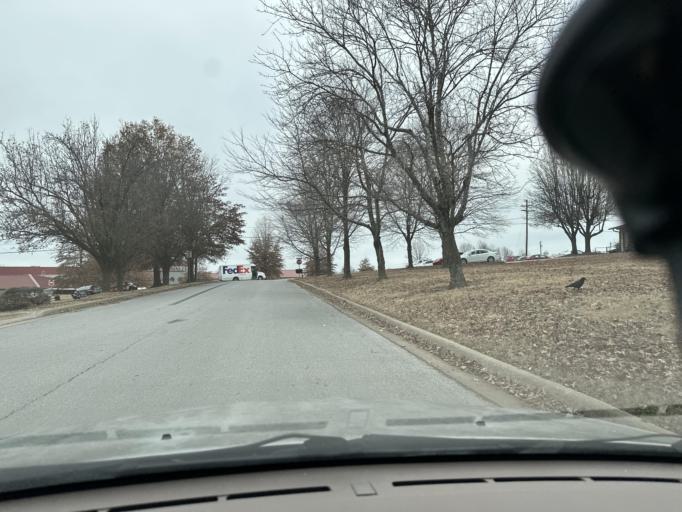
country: US
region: Arkansas
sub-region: Washington County
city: Fayetteville
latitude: 36.0871
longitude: -94.1175
